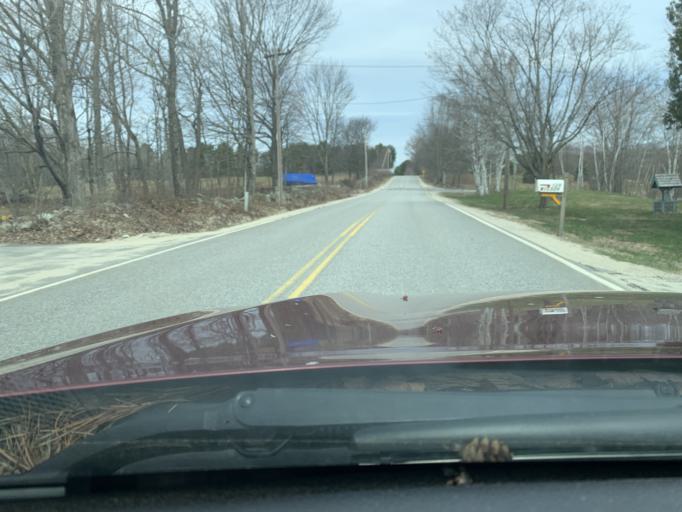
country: US
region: Maine
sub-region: Androscoggin County
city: Poland
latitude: 43.9623
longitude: -70.3912
